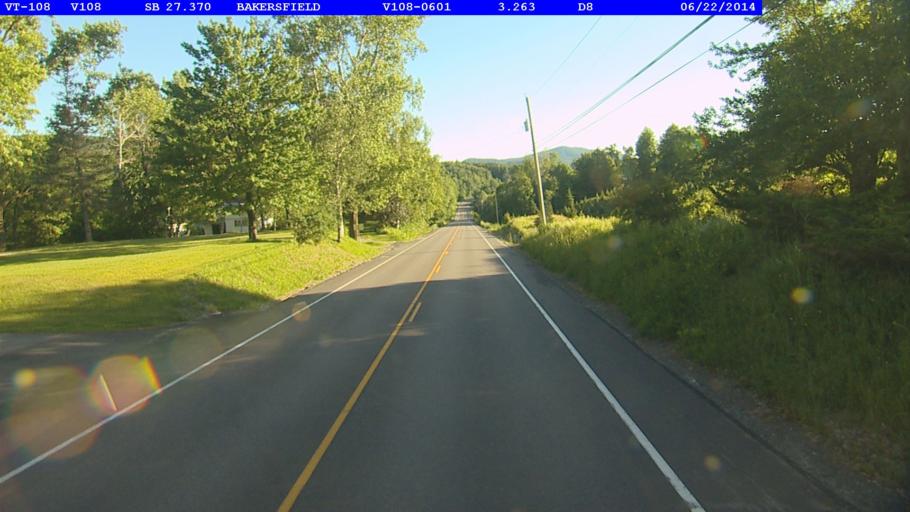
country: US
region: Vermont
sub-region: Franklin County
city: Enosburg Falls
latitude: 44.7766
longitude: -72.8045
